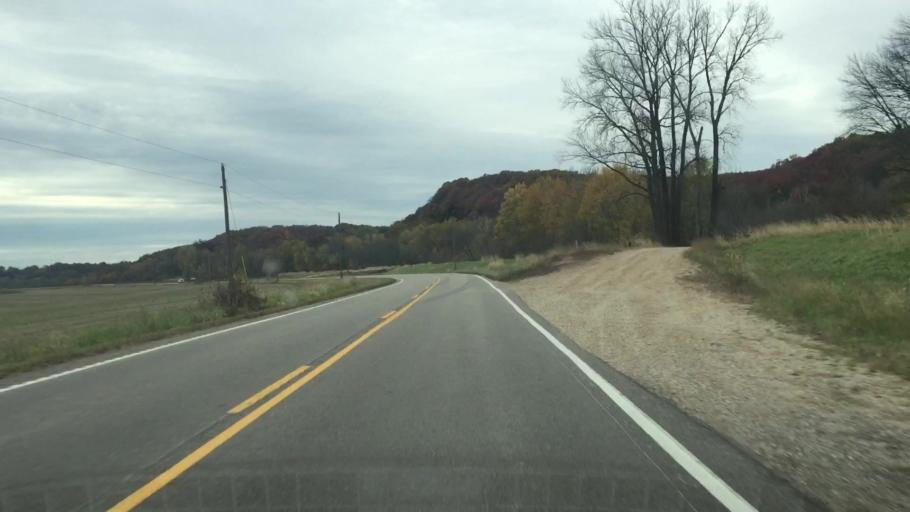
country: US
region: Missouri
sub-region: Callaway County
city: Fulton
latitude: 38.7070
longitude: -91.7814
